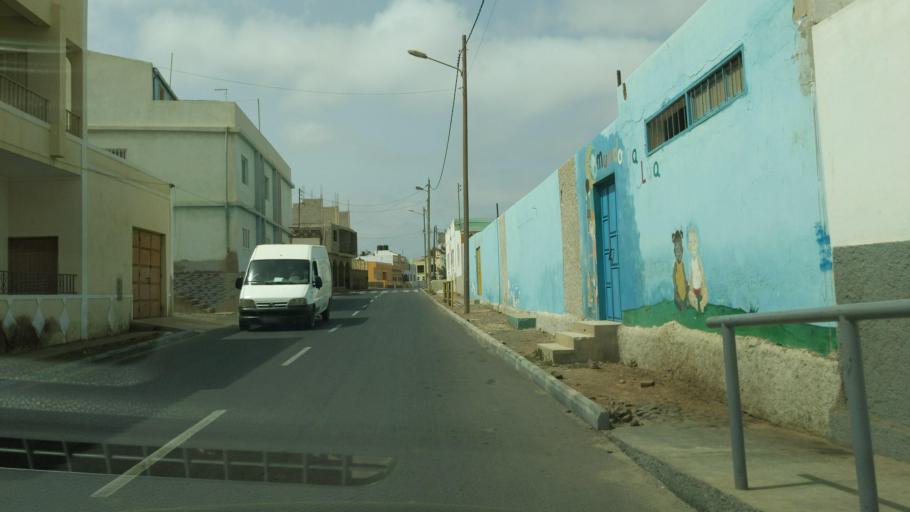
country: CV
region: Sal
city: Espargos
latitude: 16.7562
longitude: -22.9471
